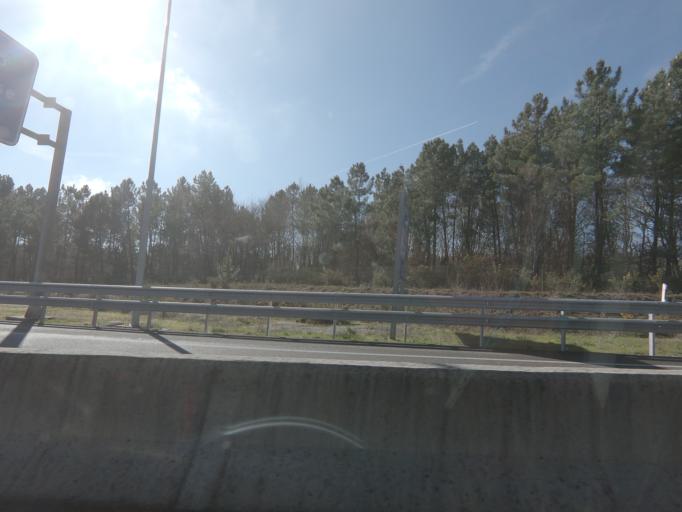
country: ES
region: Galicia
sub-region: Provincia de Ourense
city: Maside
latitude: 42.4513
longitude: -8.0267
